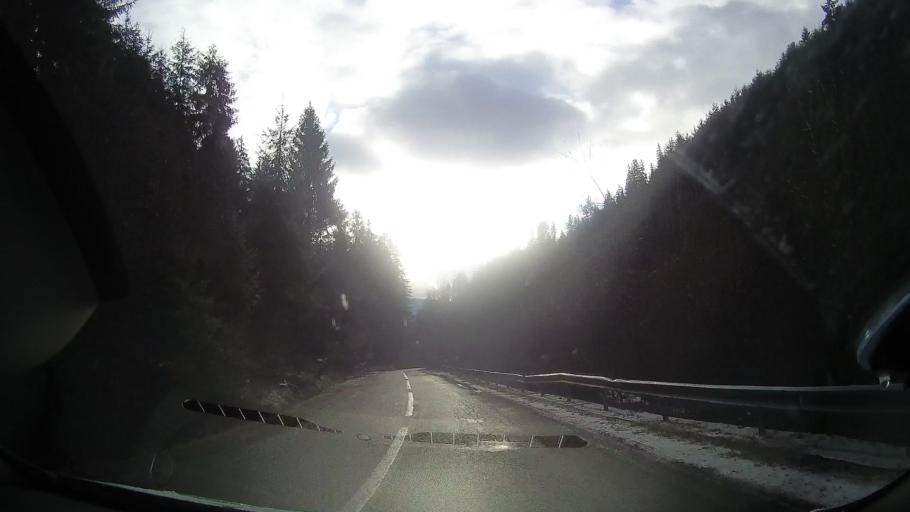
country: RO
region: Alba
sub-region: Comuna Albac
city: Albac
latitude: 46.4724
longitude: 22.9649
